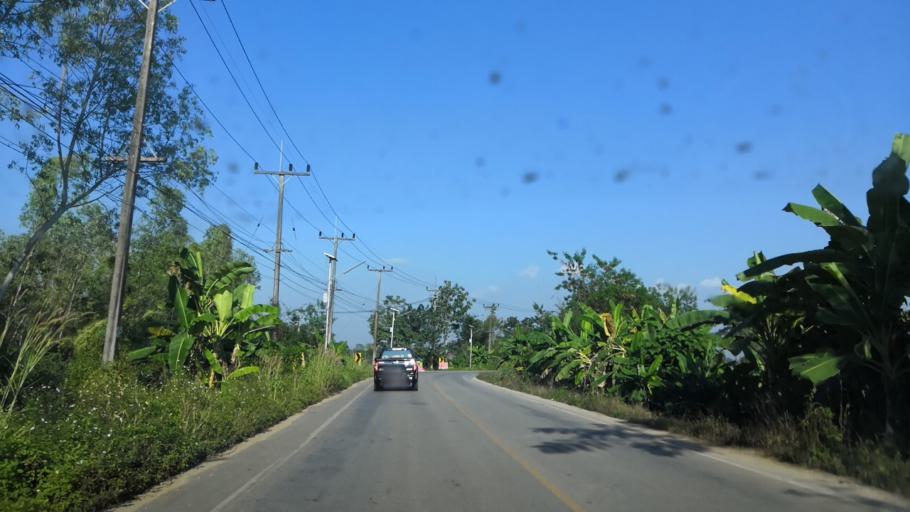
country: TH
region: Chiang Rai
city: Chiang Rai
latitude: 19.9336
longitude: 99.8797
